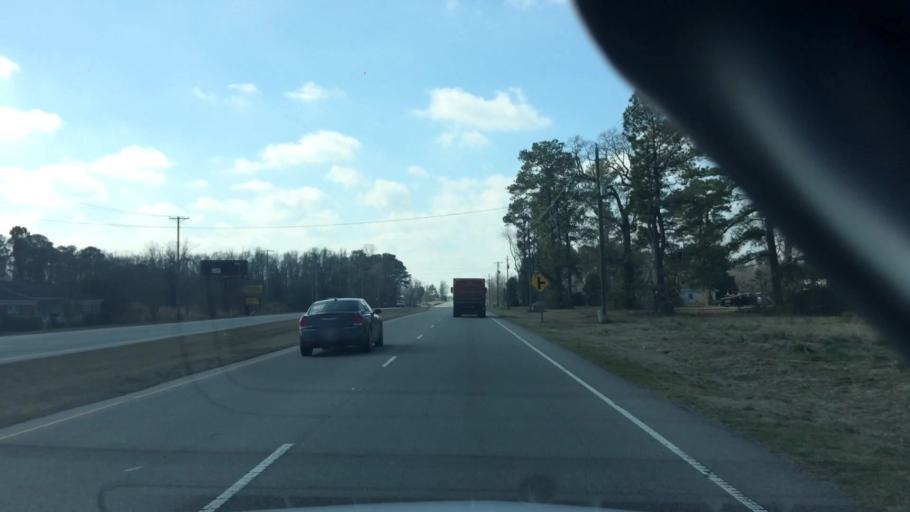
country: US
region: North Carolina
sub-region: Lenoir County
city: Kinston
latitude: 35.2953
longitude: -77.5413
